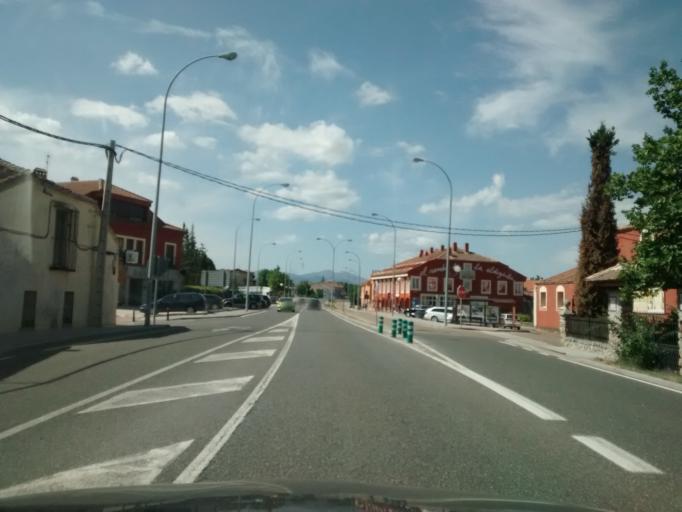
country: ES
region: Castille and Leon
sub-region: Provincia de Segovia
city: Torrecaballeros
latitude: 40.9967
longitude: -4.0214
